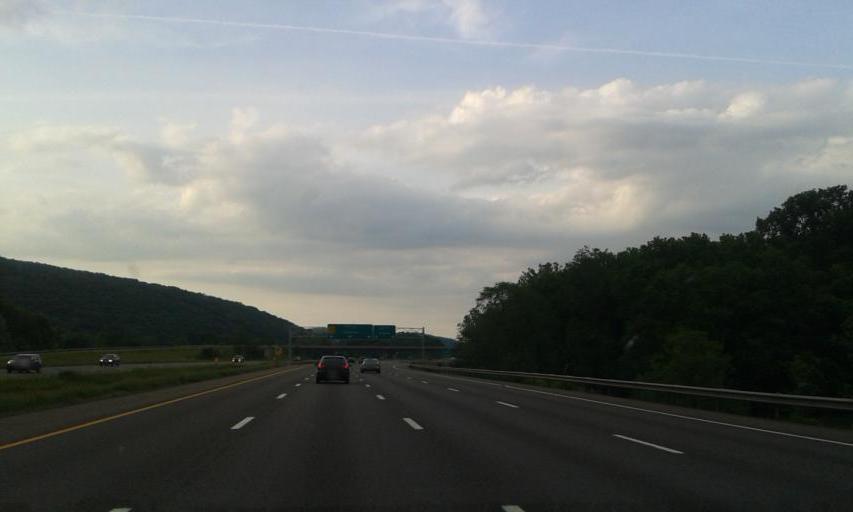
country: US
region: New York
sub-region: Broome County
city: Port Dickinson
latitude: 42.1377
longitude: -75.9023
